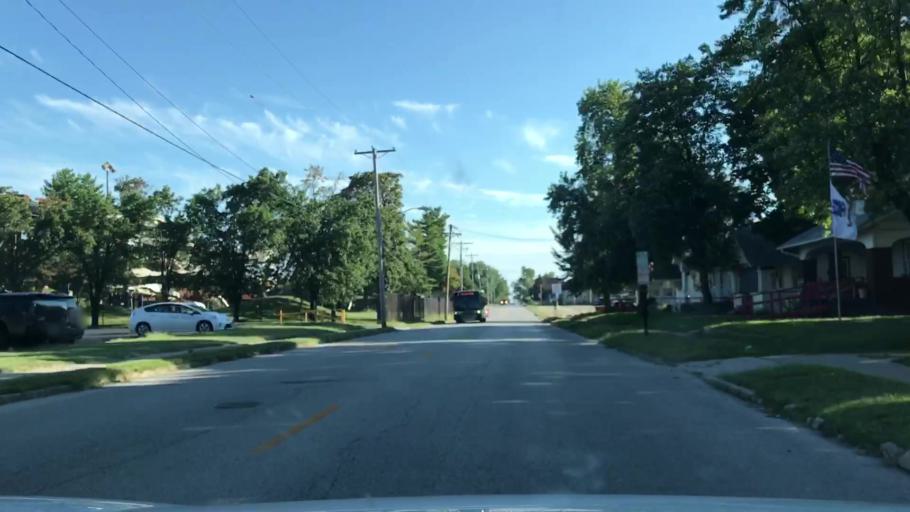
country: US
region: Illinois
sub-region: Madison County
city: Wood River
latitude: 38.8707
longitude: -90.0987
